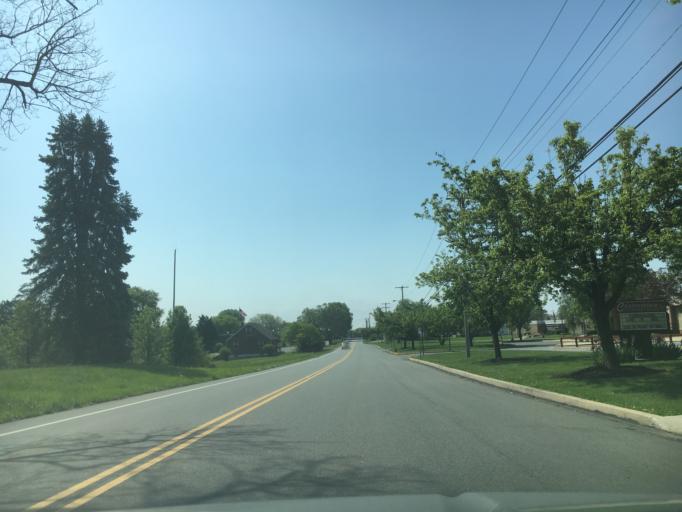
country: US
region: Pennsylvania
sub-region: Berks County
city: New Berlinville
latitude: 40.3397
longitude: -75.6271
